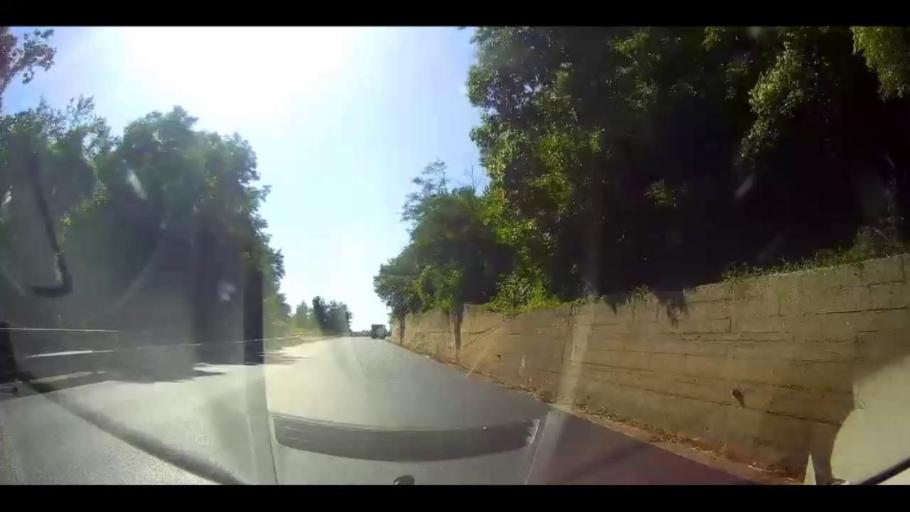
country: IT
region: Calabria
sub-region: Provincia di Cosenza
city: Celico
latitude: 39.3192
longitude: 16.3694
